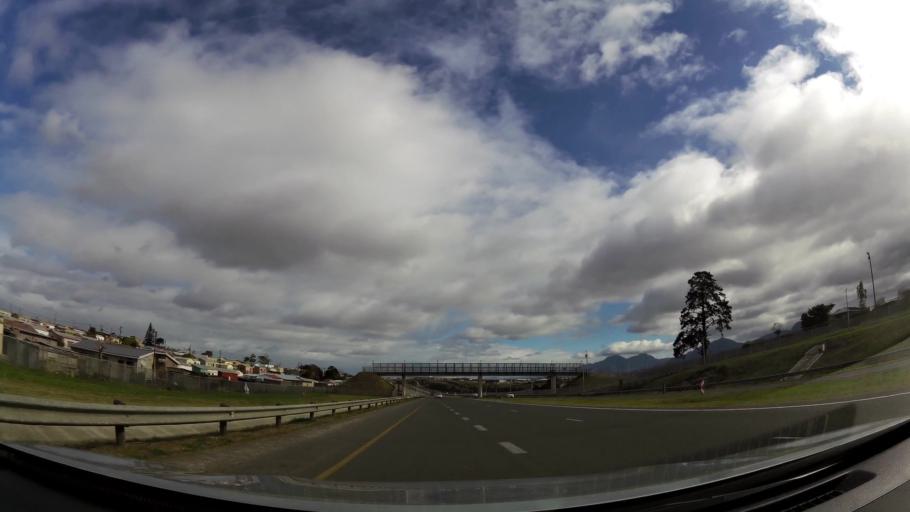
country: ZA
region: Western Cape
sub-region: Eden District Municipality
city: George
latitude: -33.9960
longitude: 22.4702
